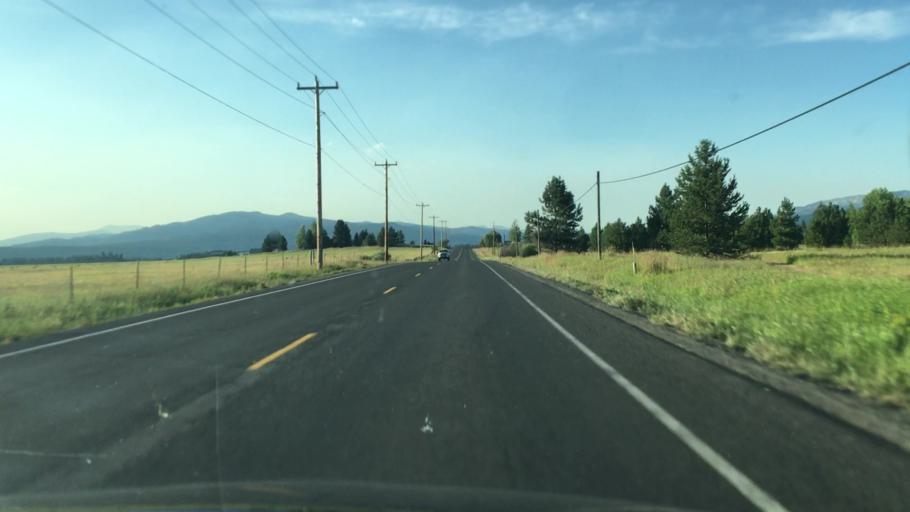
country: US
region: Idaho
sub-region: Valley County
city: McCall
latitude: 44.8762
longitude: -116.0907
